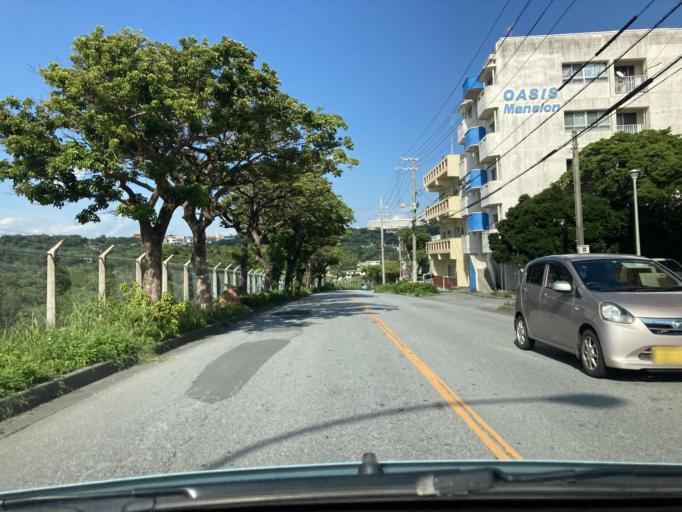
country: JP
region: Okinawa
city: Chatan
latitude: 26.2982
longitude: 127.7870
